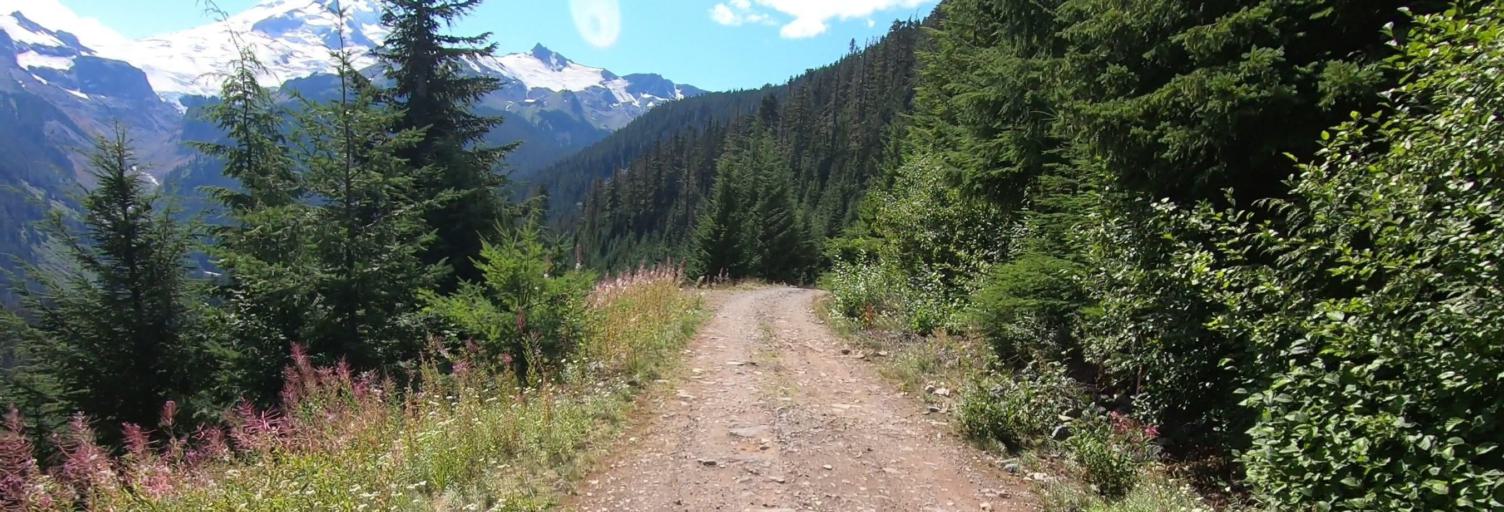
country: CA
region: British Columbia
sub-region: Fraser Valley Regional District
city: Chilliwack
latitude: 48.8643
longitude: -121.7905
